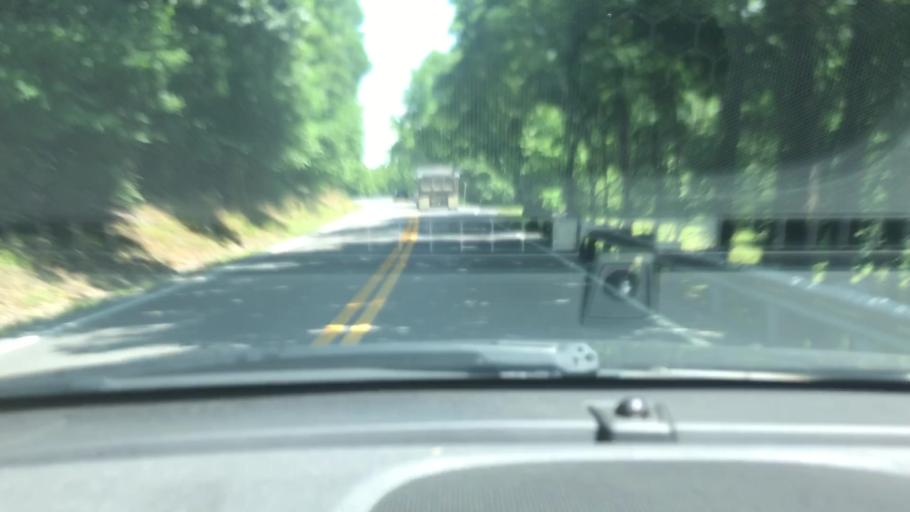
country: US
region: Tennessee
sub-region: Sumner County
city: White House
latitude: 36.4167
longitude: -86.6516
